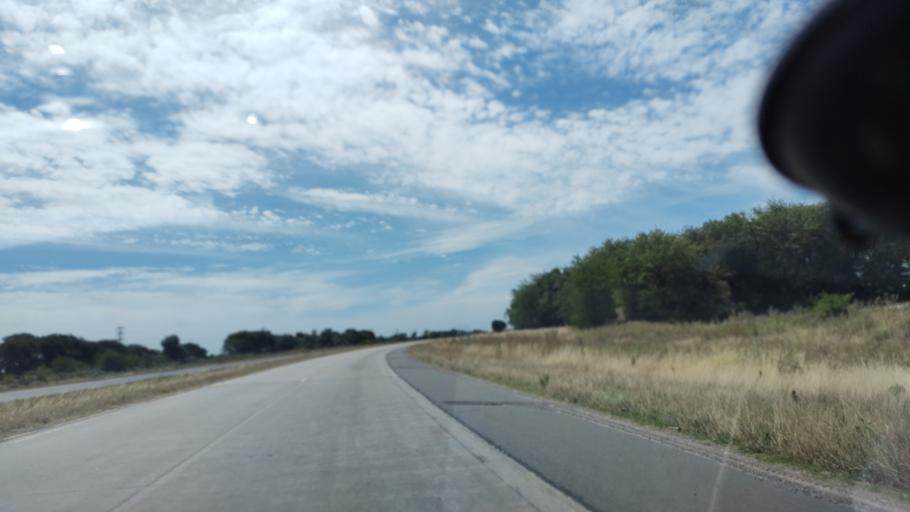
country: AR
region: Buenos Aires
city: Canuelas
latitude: -35.0566
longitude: -58.7081
